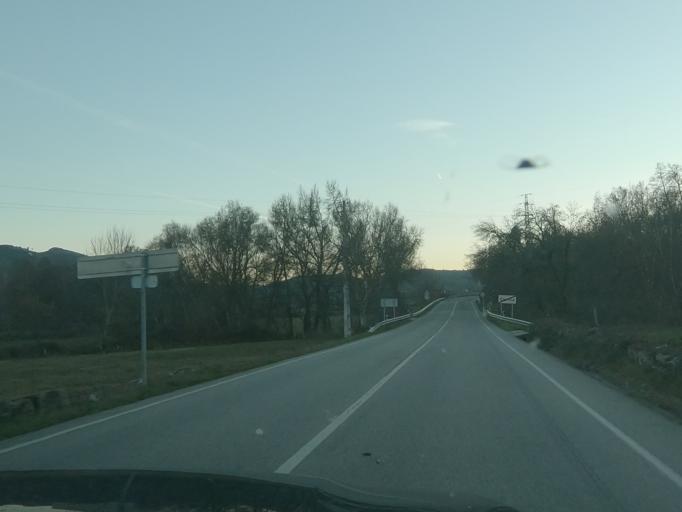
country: PT
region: Vila Real
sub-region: Vila Pouca de Aguiar
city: Vila Pouca de Aguiar
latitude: 41.4296
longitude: -7.6810
